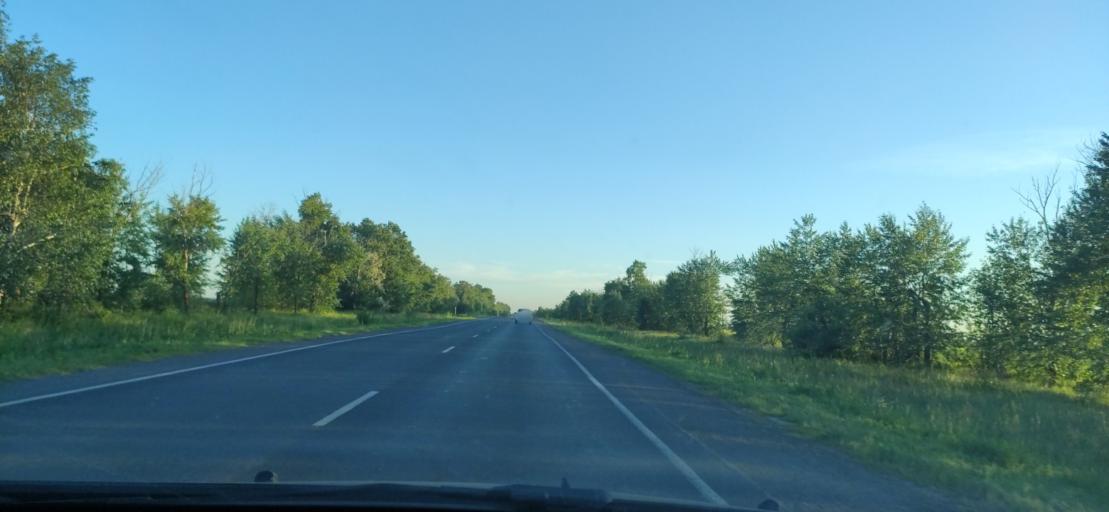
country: RU
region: Ulyanovsk
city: Cherdakly
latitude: 54.4063
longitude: 48.8708
